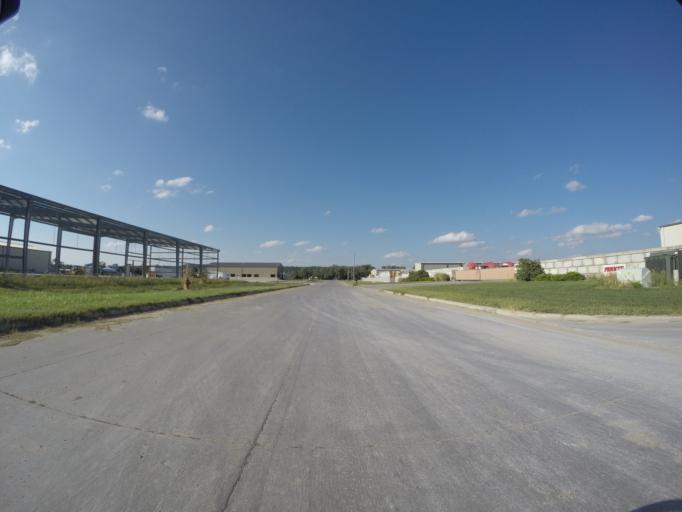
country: US
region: Kansas
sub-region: Riley County
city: Ogden
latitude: 39.1508
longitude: -96.6510
